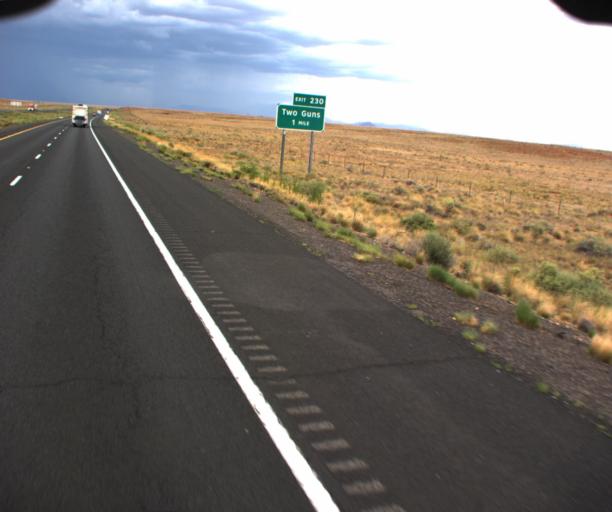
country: US
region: Arizona
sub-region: Coconino County
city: LeChee
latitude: 35.1144
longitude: -111.0687
